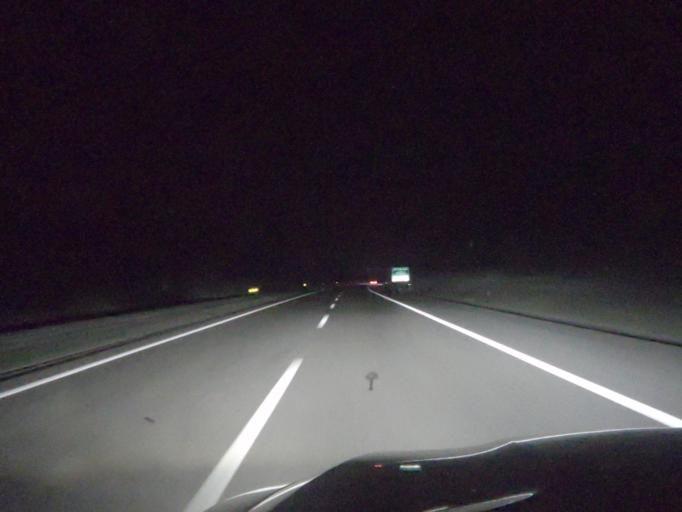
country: PT
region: Coimbra
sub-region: Soure
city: Soure
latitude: 40.0464
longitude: -8.5716
